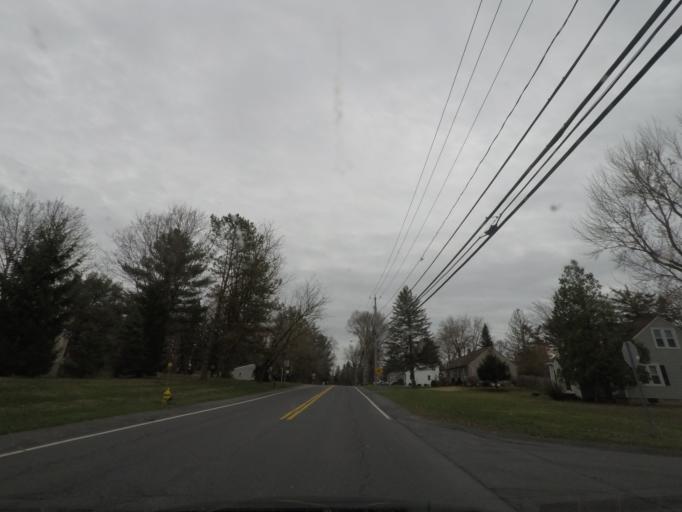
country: US
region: New York
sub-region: Albany County
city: Delmar
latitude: 42.5928
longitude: -73.8108
